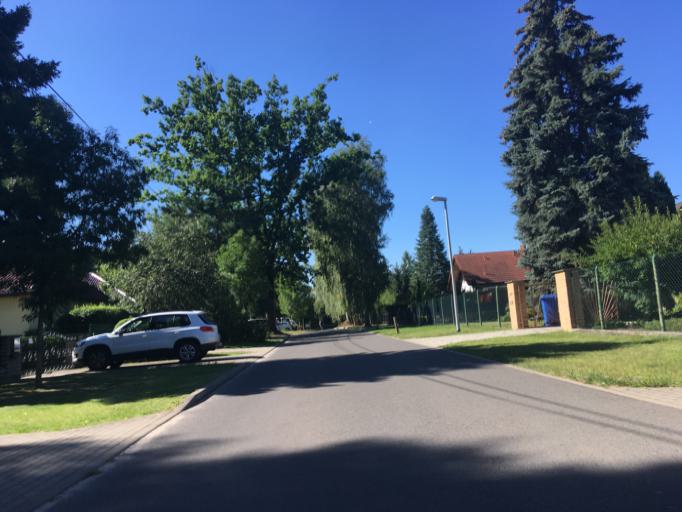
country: DE
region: Brandenburg
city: Altlandsberg
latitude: 52.5597
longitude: 13.7134
